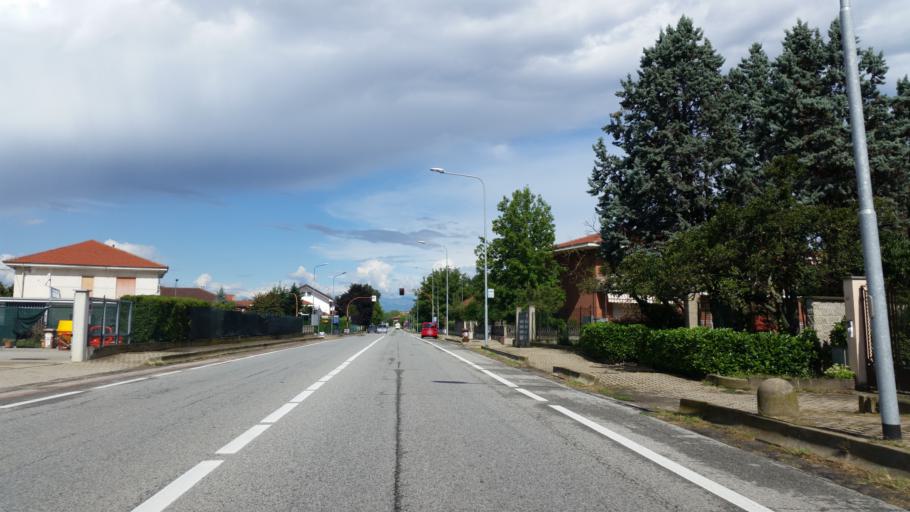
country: IT
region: Piedmont
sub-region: Provincia di Torino
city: Poirino
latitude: 44.9137
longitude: 7.8478
